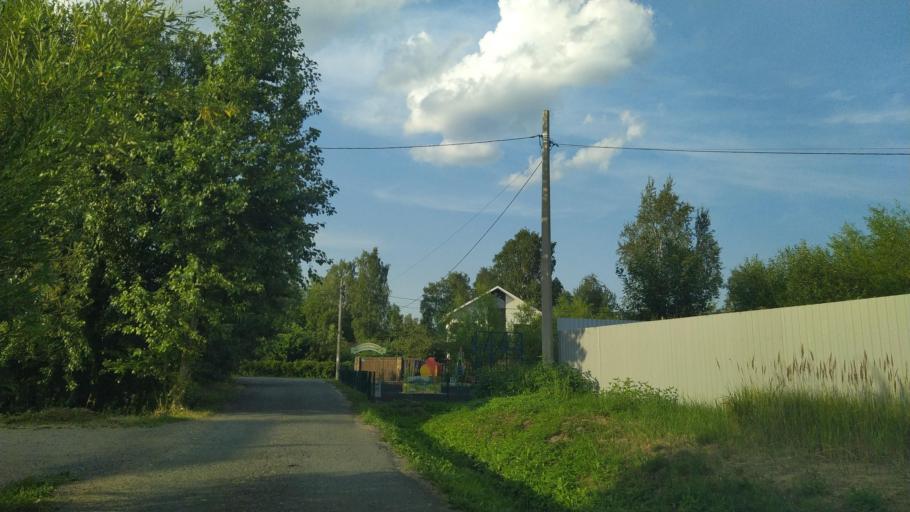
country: RU
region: St.-Petersburg
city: Lakhtinskiy
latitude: 59.9897
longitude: 30.1547
